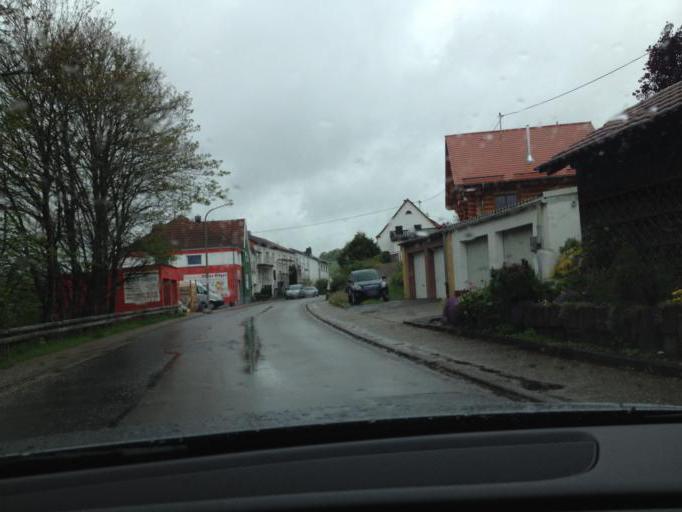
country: DE
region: Rheinland-Pfalz
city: Herchweiler
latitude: 49.4855
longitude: 7.2490
